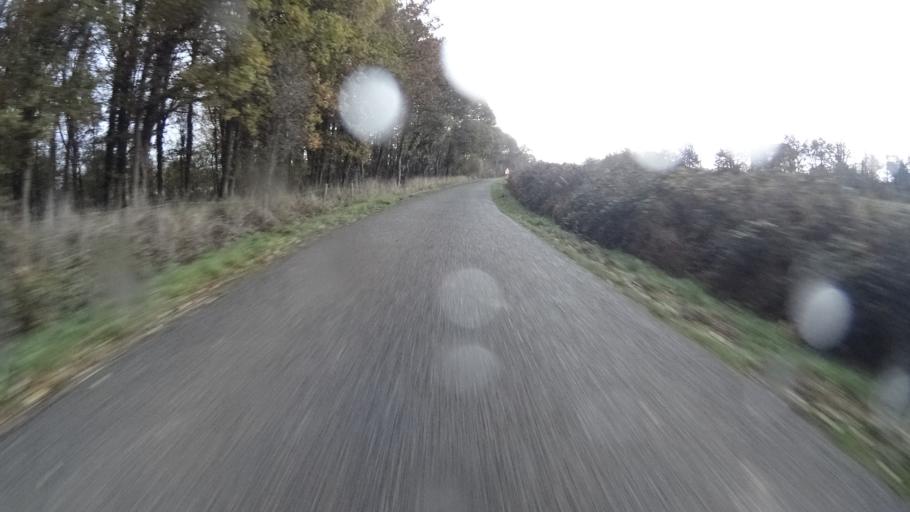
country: FR
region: Pays de la Loire
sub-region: Departement de la Loire-Atlantique
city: Avessac
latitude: 47.6659
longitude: -1.9979
